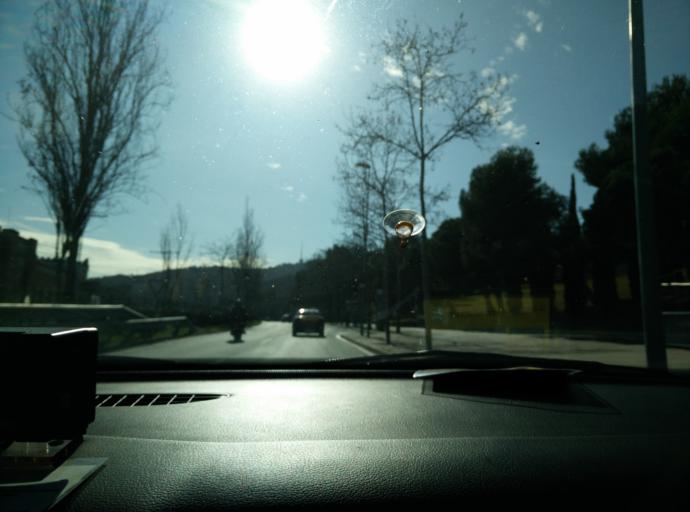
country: ES
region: Catalonia
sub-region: Provincia de Barcelona
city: Horta-Guinardo
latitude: 41.4375
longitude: 2.1504
